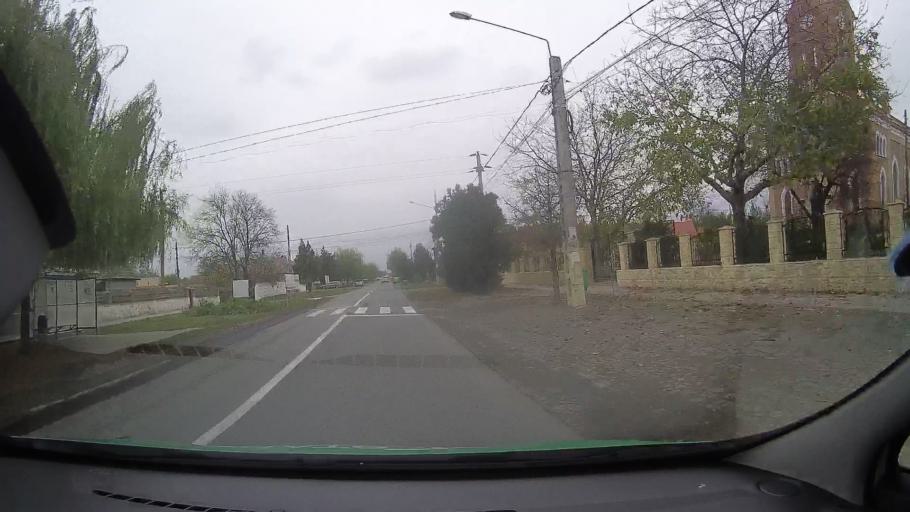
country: RO
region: Constanta
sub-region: Comuna Mihail Kogalniceanu
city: Mihail Kogalniceanu
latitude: 44.3732
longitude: 28.4642
